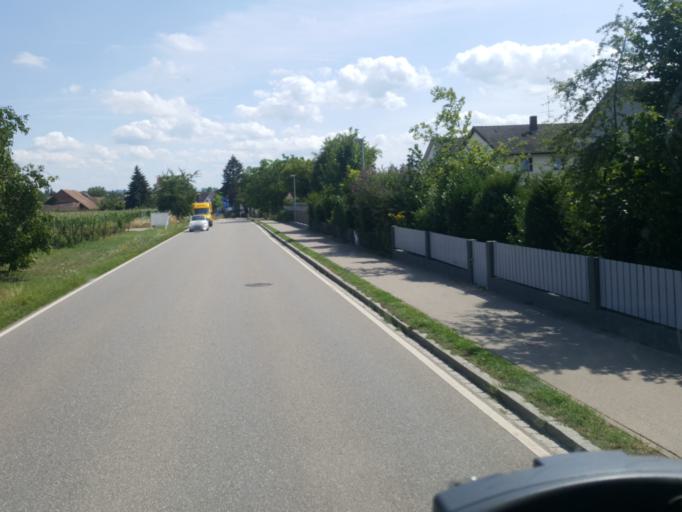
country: DE
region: Baden-Wuerttemberg
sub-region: Freiburg Region
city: Eimeldingen
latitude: 47.6358
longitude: 7.5928
